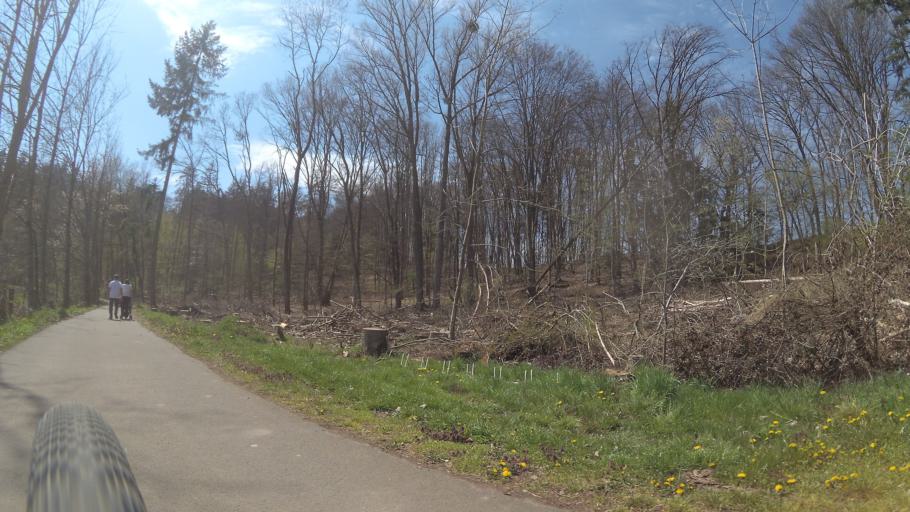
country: DE
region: Rheinland-Pfalz
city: Brucken
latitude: 49.4242
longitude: 7.3780
